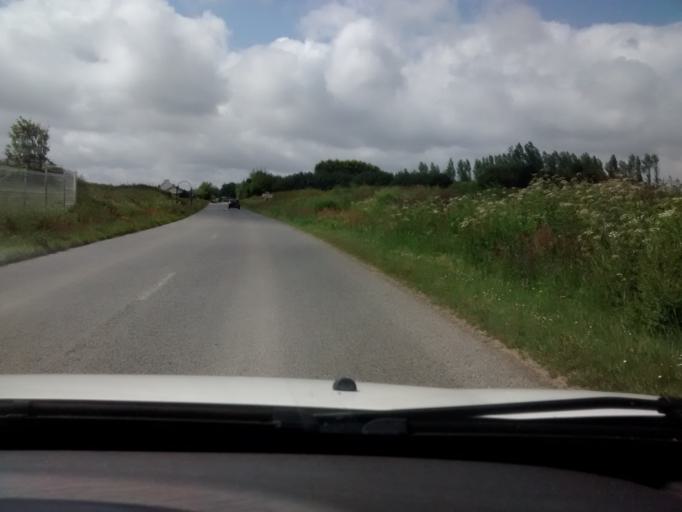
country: FR
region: Brittany
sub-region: Departement des Cotes-d'Armor
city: Penvenan
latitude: 48.8052
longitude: -3.3078
